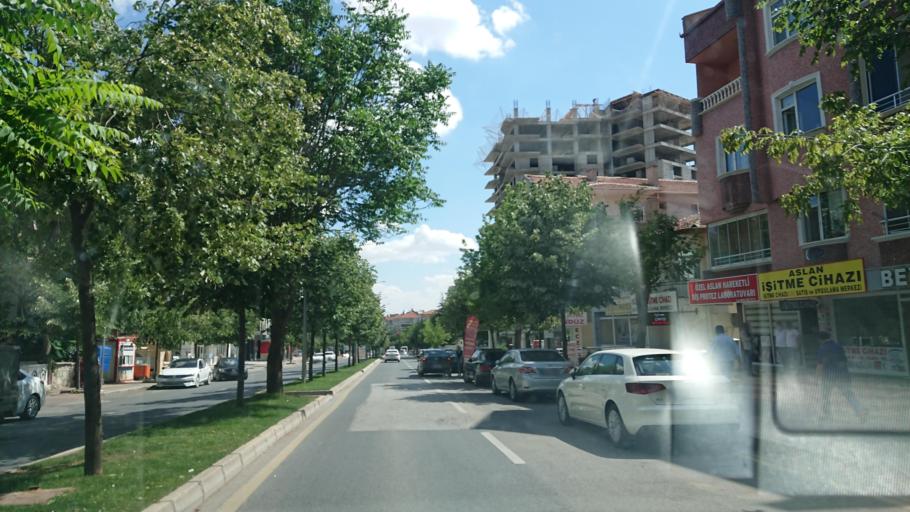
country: TR
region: Kirsehir
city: Kirsehir
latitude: 39.1566
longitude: 34.1598
